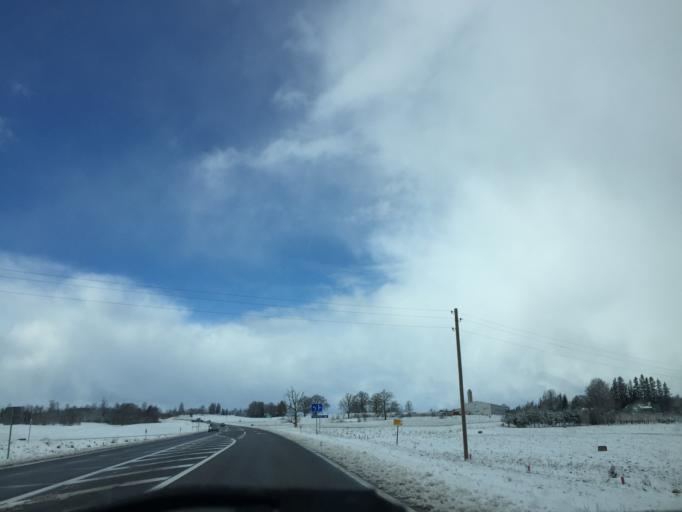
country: LV
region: Talsu Rajons
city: Talsi
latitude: 57.1815
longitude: 22.6352
